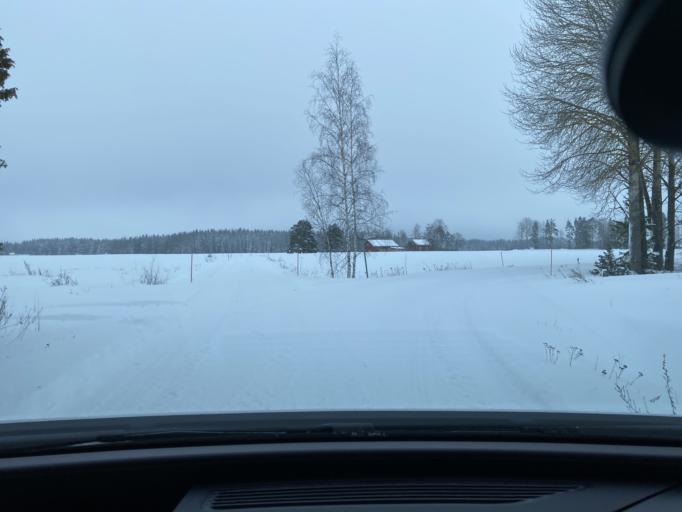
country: FI
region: Pirkanmaa
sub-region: Lounais-Pirkanmaa
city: Punkalaidun
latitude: 61.1253
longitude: 23.0824
